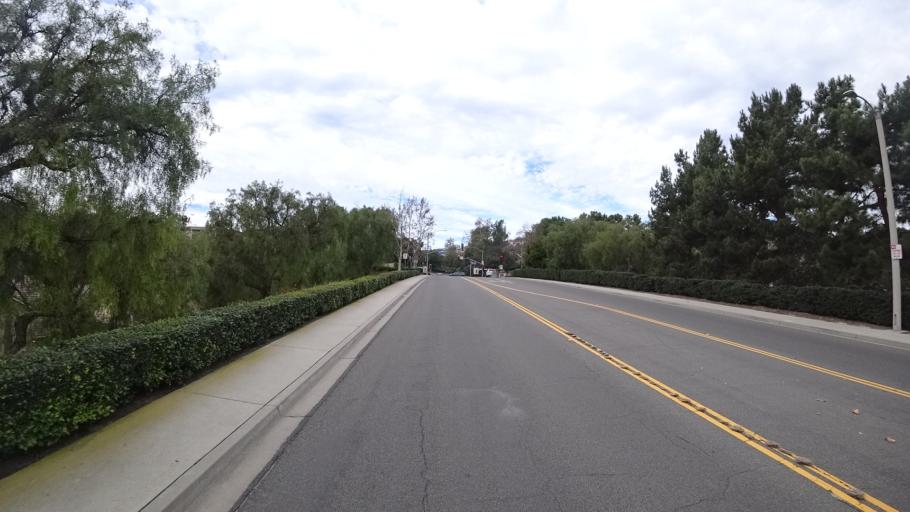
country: US
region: California
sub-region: Orange County
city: Aliso Viejo
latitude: 33.5688
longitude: -117.7353
